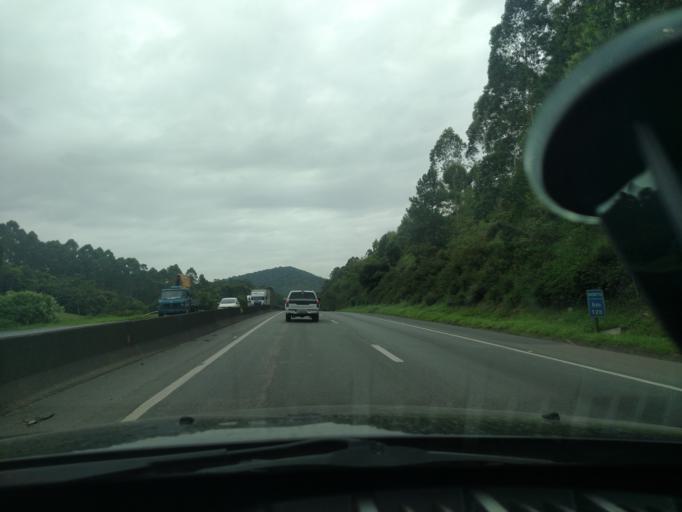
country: BR
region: Santa Catarina
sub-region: Balneario Camboriu
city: Balneario Camboriu
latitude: -26.9730
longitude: -48.6829
